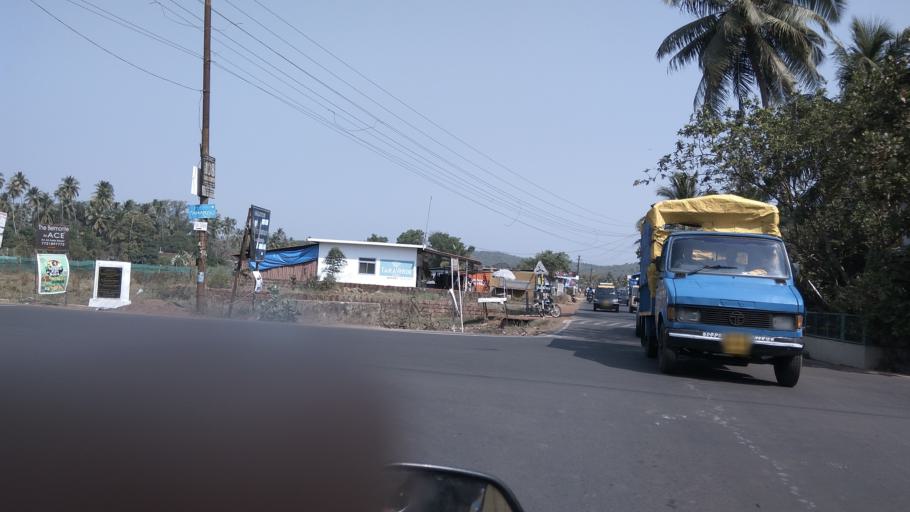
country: IN
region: Goa
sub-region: North Goa
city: Vagator
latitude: 15.5928
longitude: 73.7596
